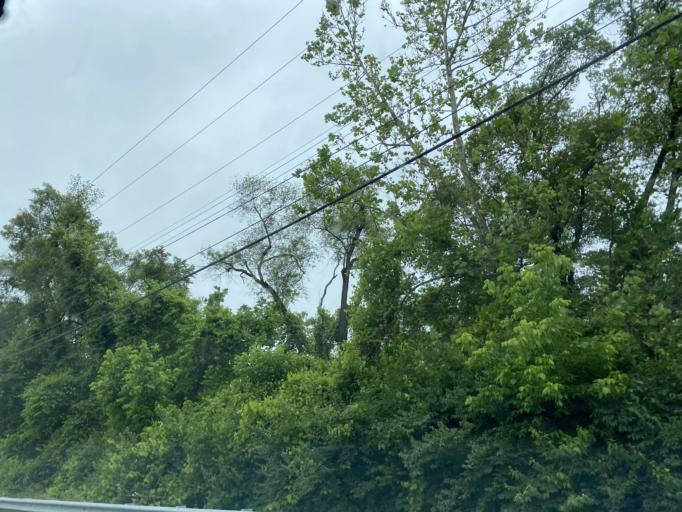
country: US
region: Kentucky
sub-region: Campbell County
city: Bellevue
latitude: 39.0996
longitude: -84.4861
